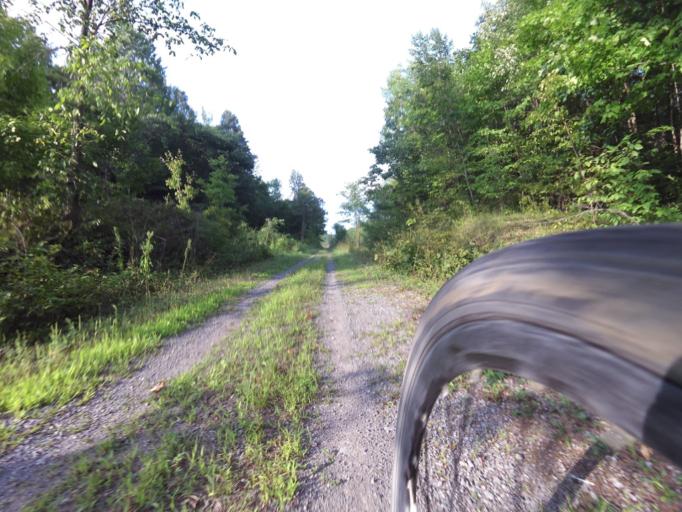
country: CA
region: Ontario
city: Kingston
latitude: 44.4902
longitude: -76.4540
